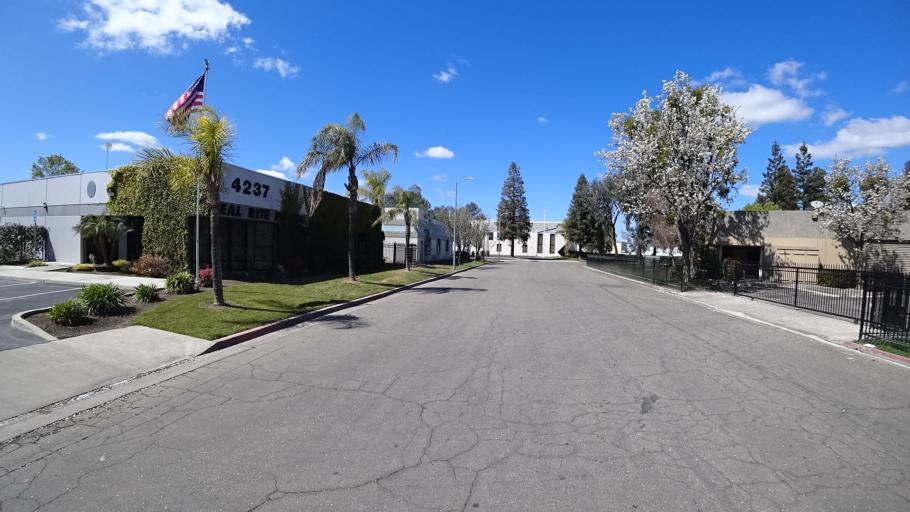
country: US
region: California
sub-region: Fresno County
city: West Park
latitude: 36.7957
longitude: -119.8669
